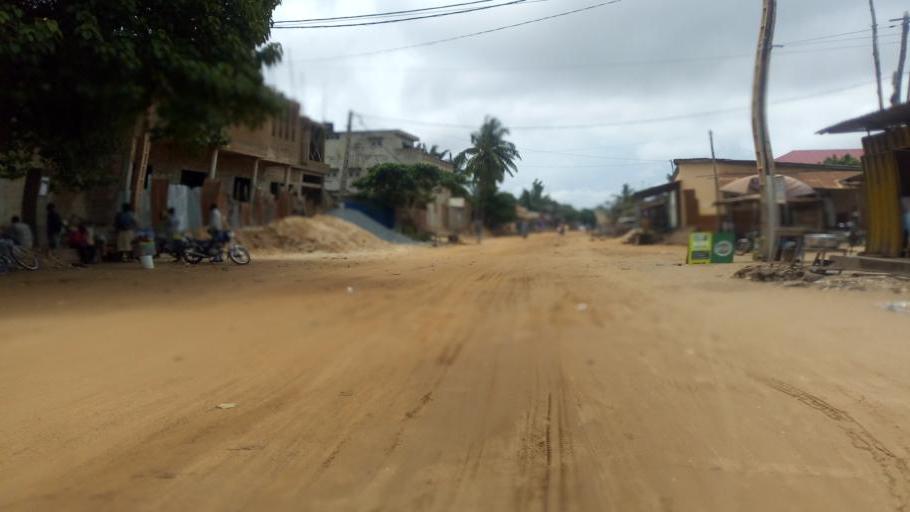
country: TG
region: Maritime
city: Lome
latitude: 6.1776
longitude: 1.1686
